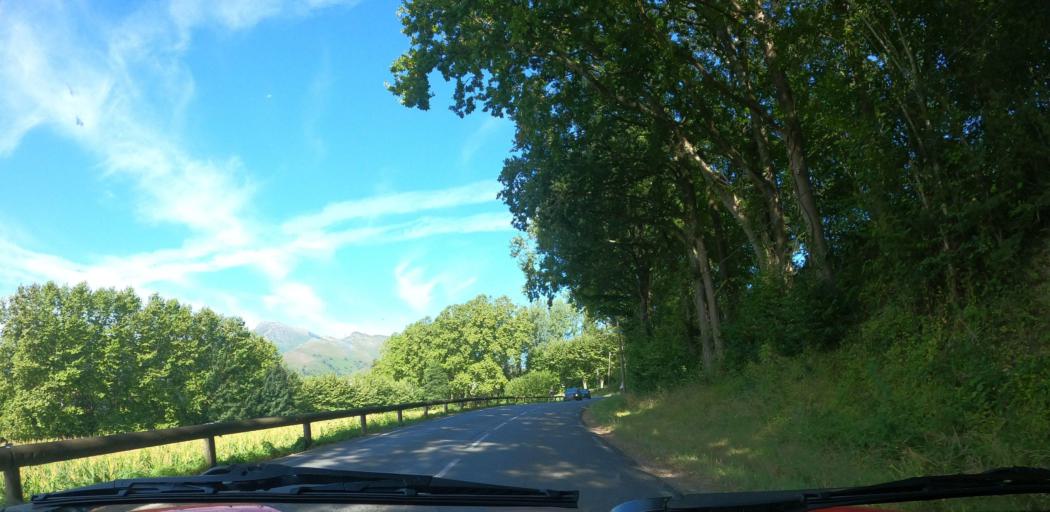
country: FR
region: Aquitaine
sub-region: Departement des Pyrenees-Atlantiques
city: Sare
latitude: 43.3095
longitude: -1.5700
